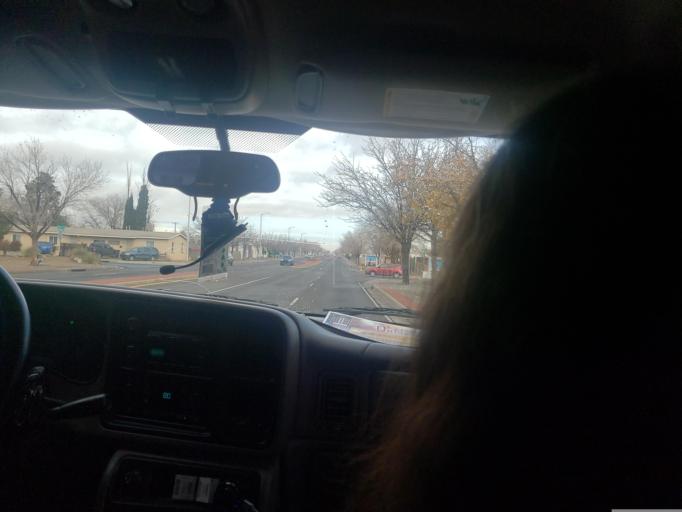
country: US
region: New Mexico
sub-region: Bernalillo County
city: Albuquerque
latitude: 35.0608
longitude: -106.5862
